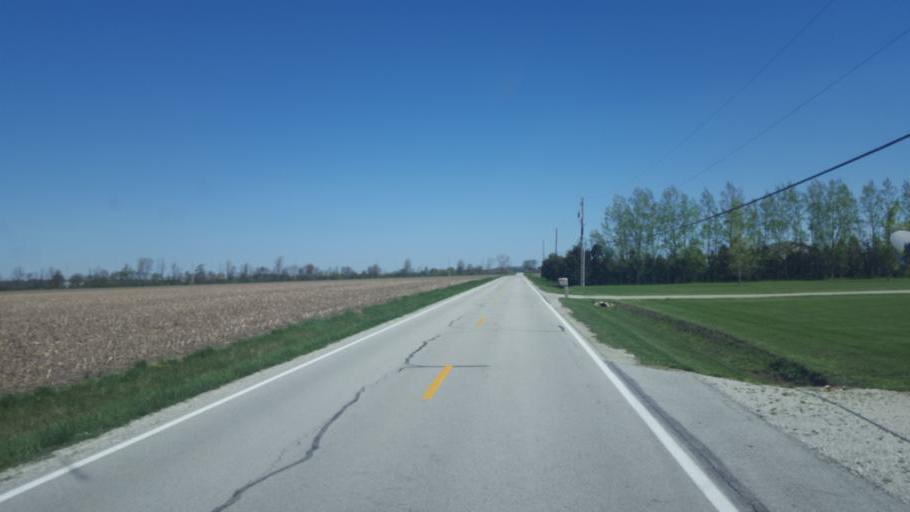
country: US
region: Ohio
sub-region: Sandusky County
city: Stony Prairie
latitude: 41.2961
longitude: -83.1973
